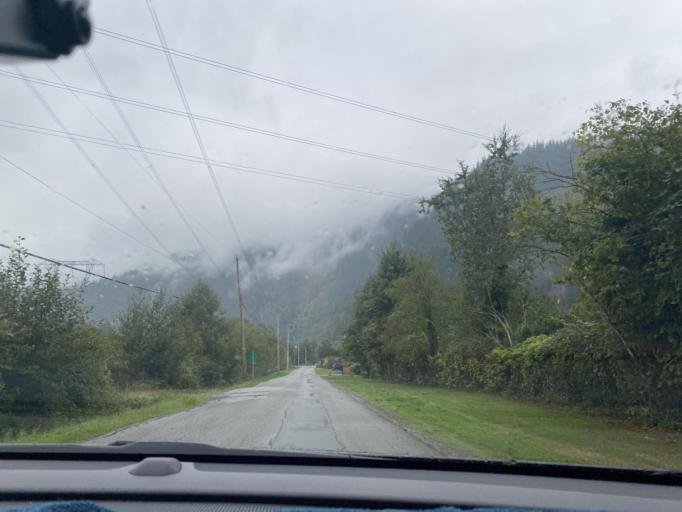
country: CA
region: British Columbia
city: Agassiz
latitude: 49.2805
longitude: -121.7793
